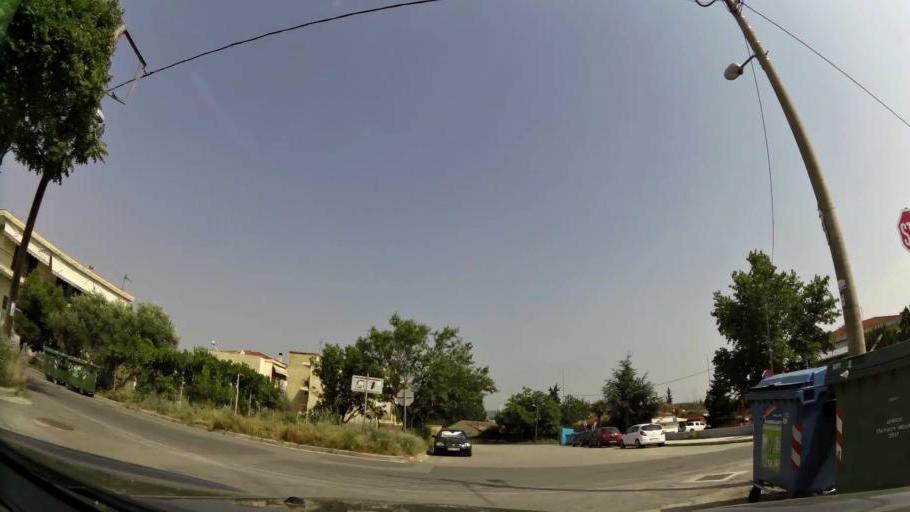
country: GR
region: Central Macedonia
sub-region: Nomos Thessalonikis
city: Efkarpia
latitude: 40.6809
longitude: 22.9441
